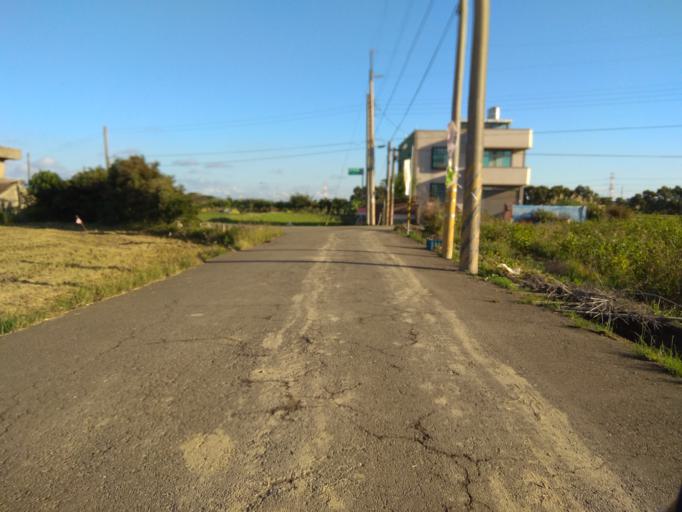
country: TW
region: Taiwan
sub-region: Hsinchu
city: Zhubei
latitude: 24.9939
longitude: 121.0534
